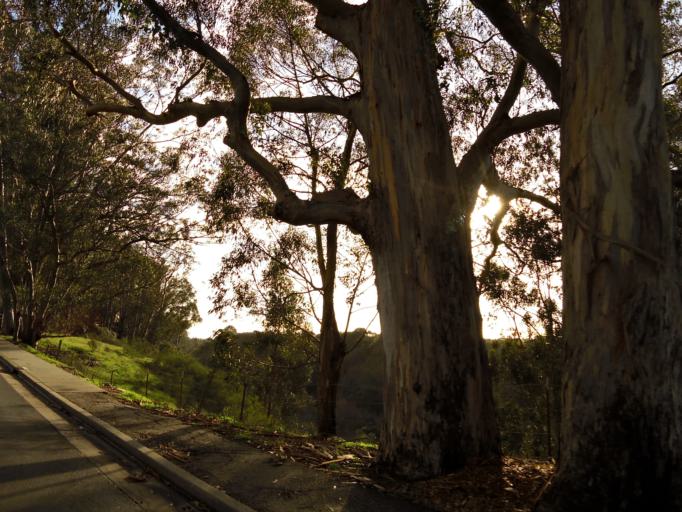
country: US
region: California
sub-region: Santa Cruz County
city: Santa Cruz
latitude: 36.9689
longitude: -122.0585
